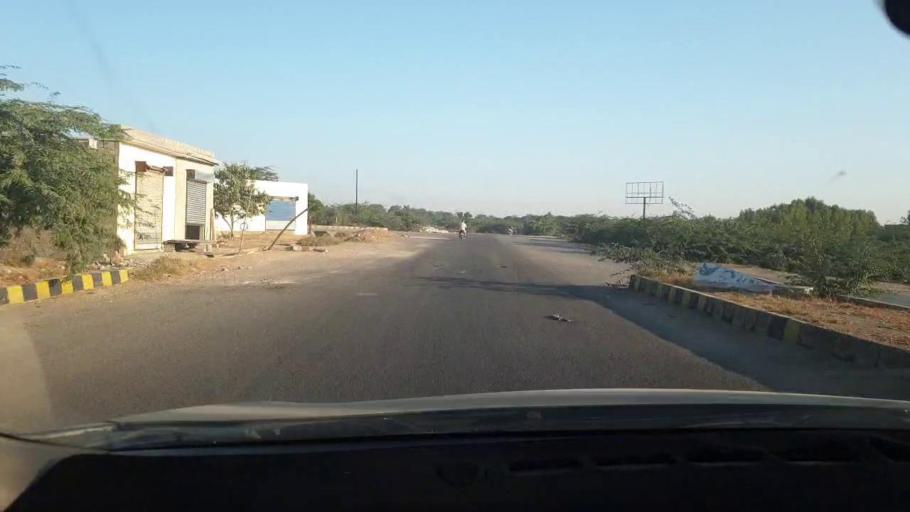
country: PK
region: Sindh
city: Malir Cantonment
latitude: 25.0496
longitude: 67.1816
